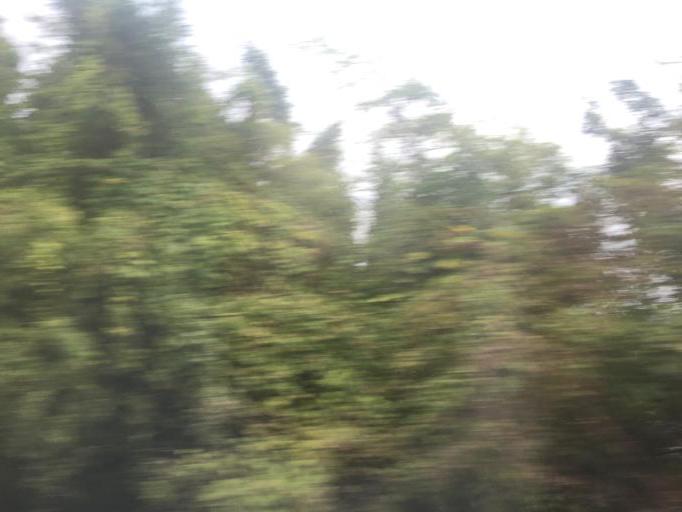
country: JP
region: Tokyo
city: Fussa
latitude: 35.7790
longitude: 139.3445
